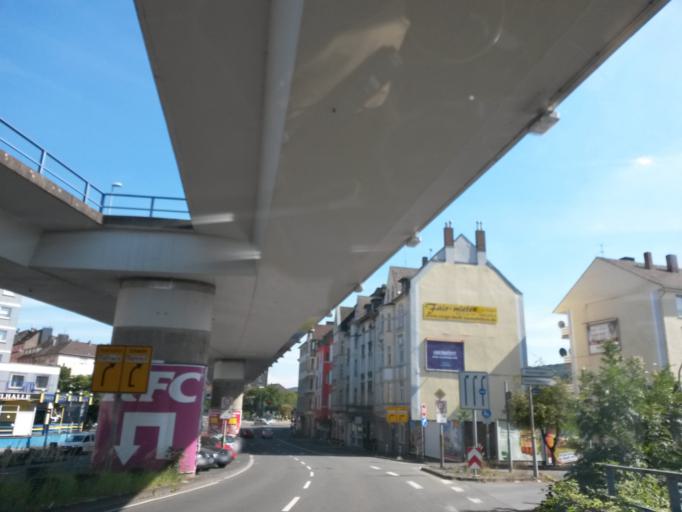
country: DE
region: North Rhine-Westphalia
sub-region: Regierungsbezirk Arnsberg
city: Hagen
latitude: 51.3657
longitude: 7.4618
